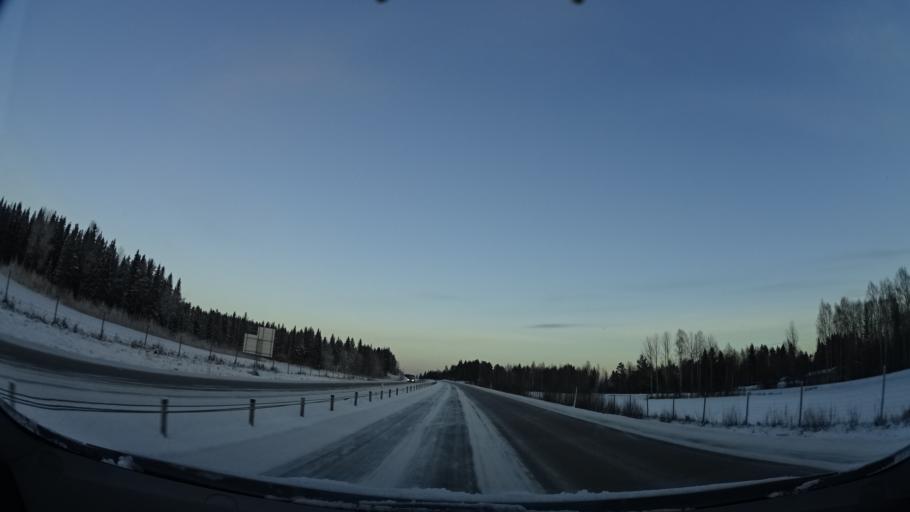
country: SE
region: Vaesterbotten
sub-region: Skelleftea Kommun
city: Kage
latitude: 64.8566
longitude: 21.0052
